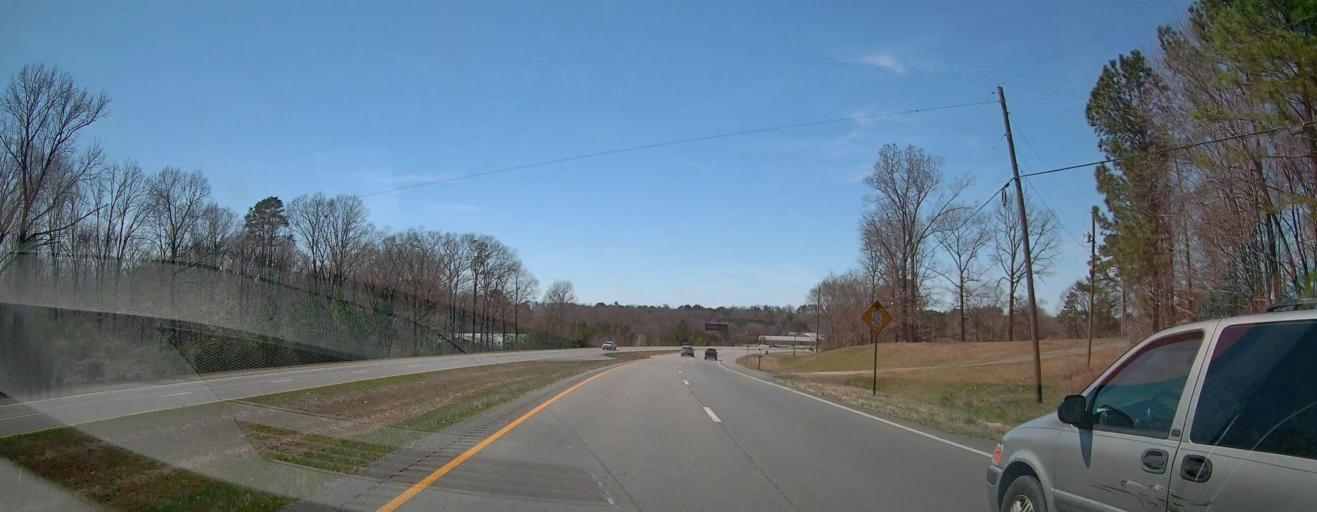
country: US
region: Alabama
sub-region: Blount County
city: Blountsville
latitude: 34.1631
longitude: -86.5057
